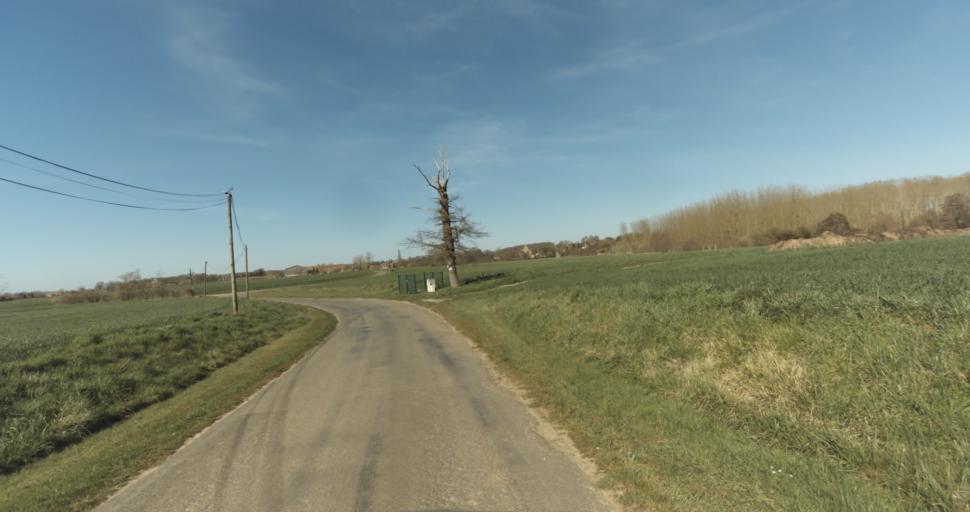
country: FR
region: Lower Normandy
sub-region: Departement du Calvados
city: Saint-Pierre-sur-Dives
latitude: 49.0454
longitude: -0.0265
